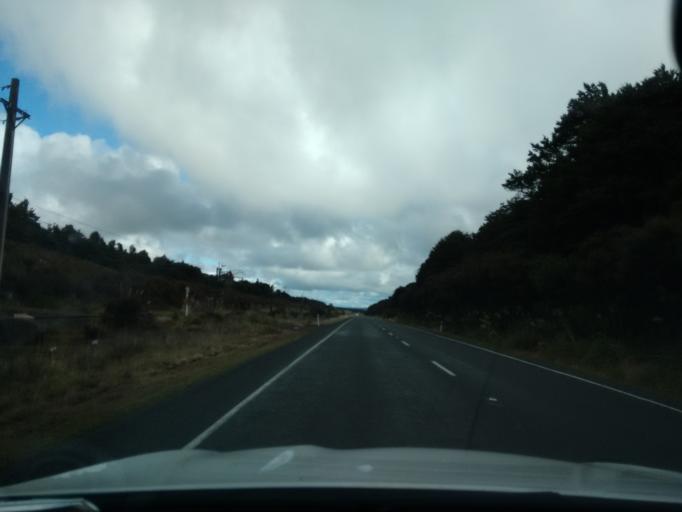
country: NZ
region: Manawatu-Wanganui
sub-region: Ruapehu District
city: Waiouru
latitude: -39.3104
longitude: 175.3891
